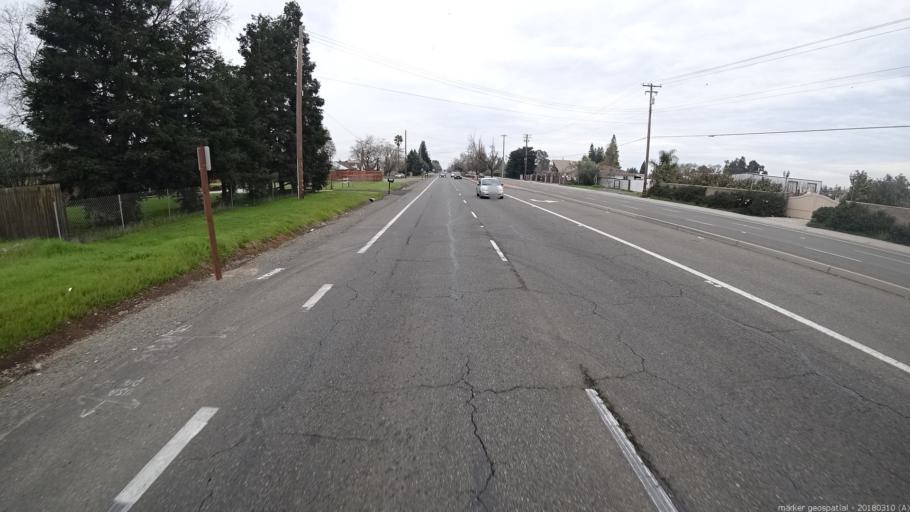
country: US
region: California
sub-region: Sacramento County
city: Vineyard
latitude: 38.4722
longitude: -121.3718
